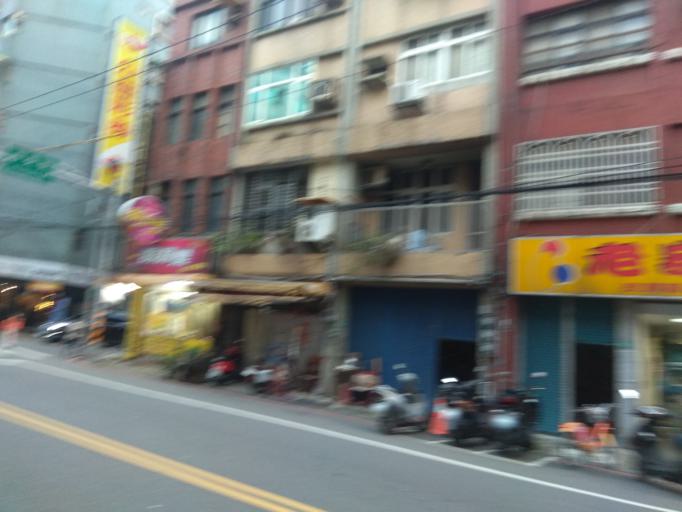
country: TW
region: Taiwan
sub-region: Taoyuan
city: Taoyuan
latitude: 24.9966
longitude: 121.3169
